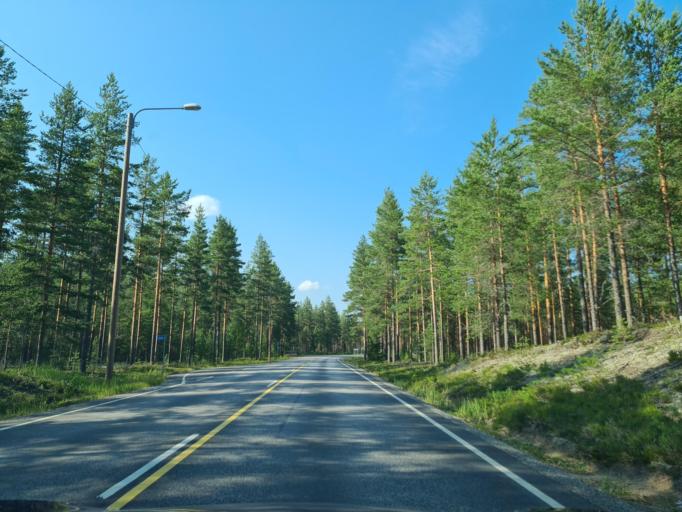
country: FI
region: Satakunta
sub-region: Pohjois-Satakunta
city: Karvia
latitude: 62.0722
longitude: 22.5071
